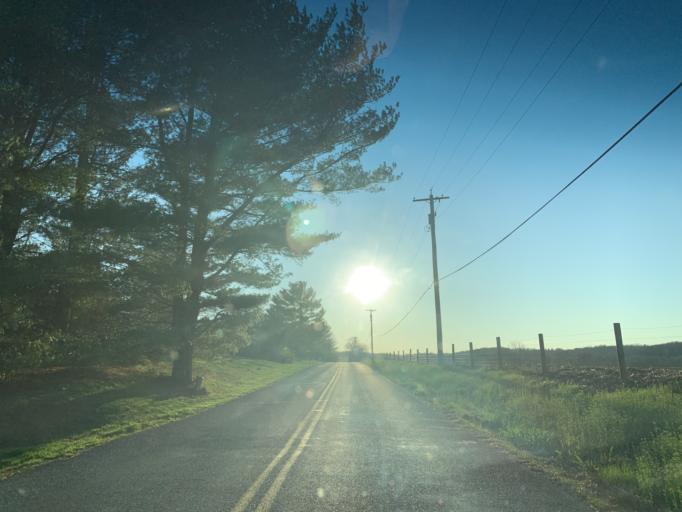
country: US
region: Maryland
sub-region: Harford County
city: South Bel Air
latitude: 39.5956
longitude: -76.2687
